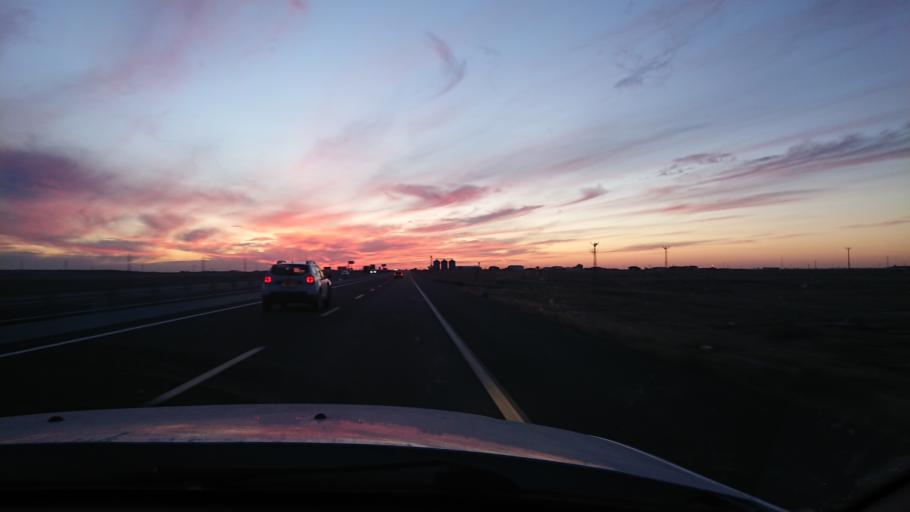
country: TR
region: Aksaray
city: Yesilova
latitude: 38.3305
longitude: 33.9070
